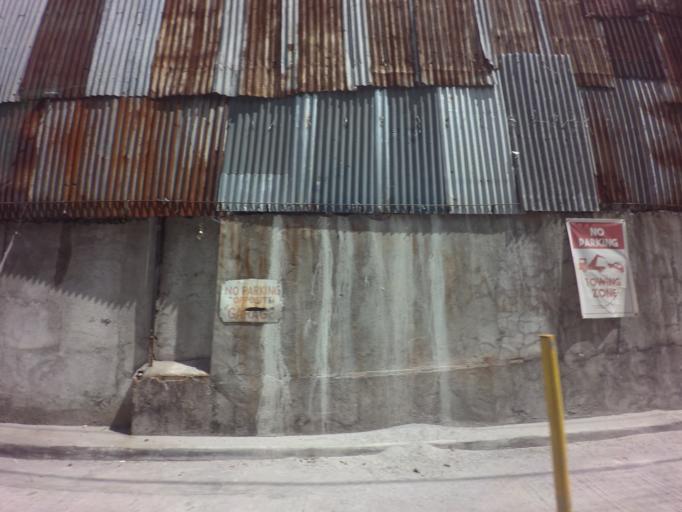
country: PH
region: Metro Manila
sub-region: Makati City
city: Makati City
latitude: 14.5521
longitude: 120.9932
